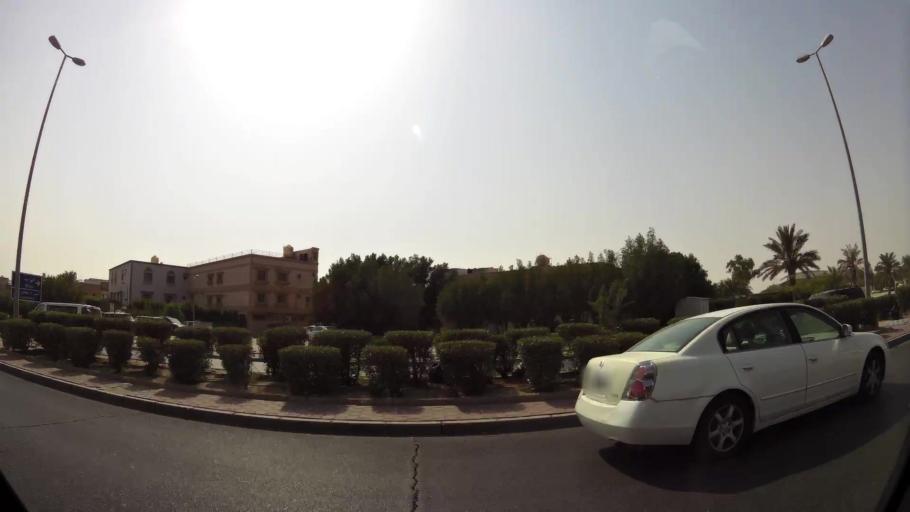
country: KW
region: Muhafazat al Jahra'
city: Al Jahra'
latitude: 29.3429
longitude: 47.6667
